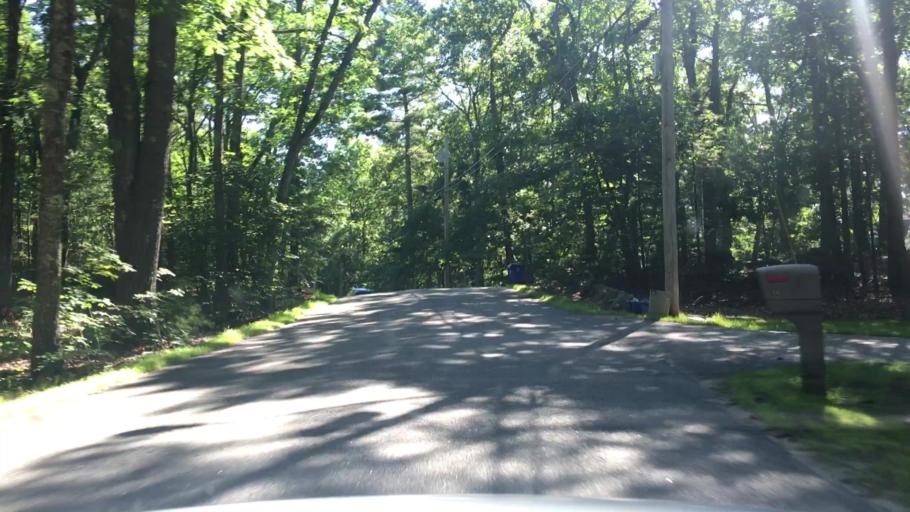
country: US
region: New Hampshire
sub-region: Rockingham County
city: Exeter
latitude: 43.0205
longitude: -70.9749
